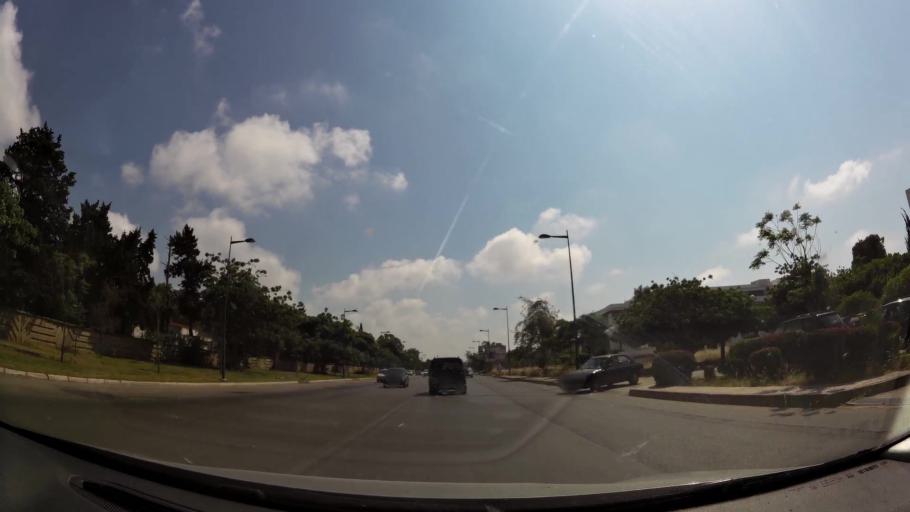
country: MA
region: Rabat-Sale-Zemmour-Zaer
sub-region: Rabat
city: Rabat
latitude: 33.9792
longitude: -6.8664
